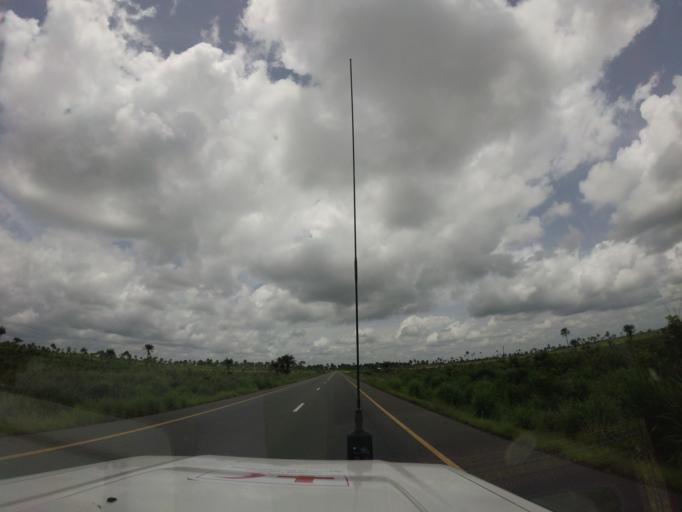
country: SL
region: Northern Province
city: Mange
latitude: 9.0110
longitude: -12.8640
